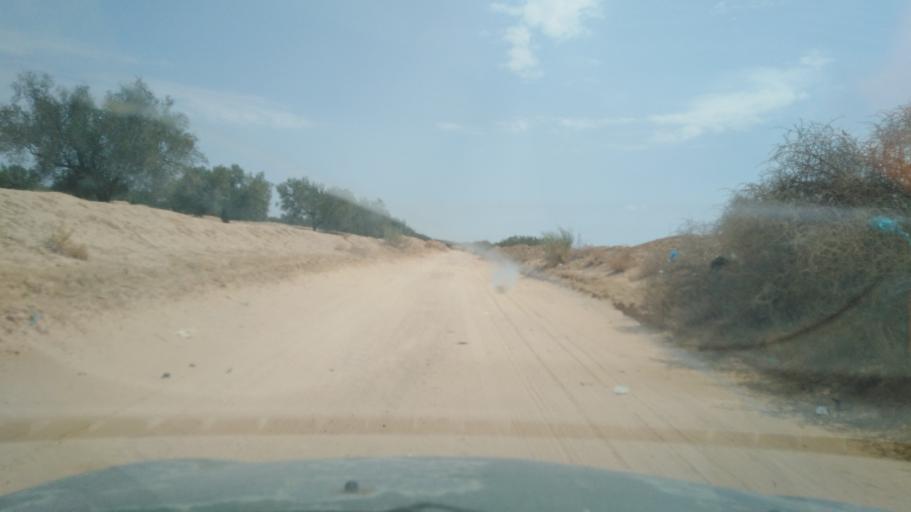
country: TN
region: Safaqis
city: Sfax
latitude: 34.7384
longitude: 10.5567
